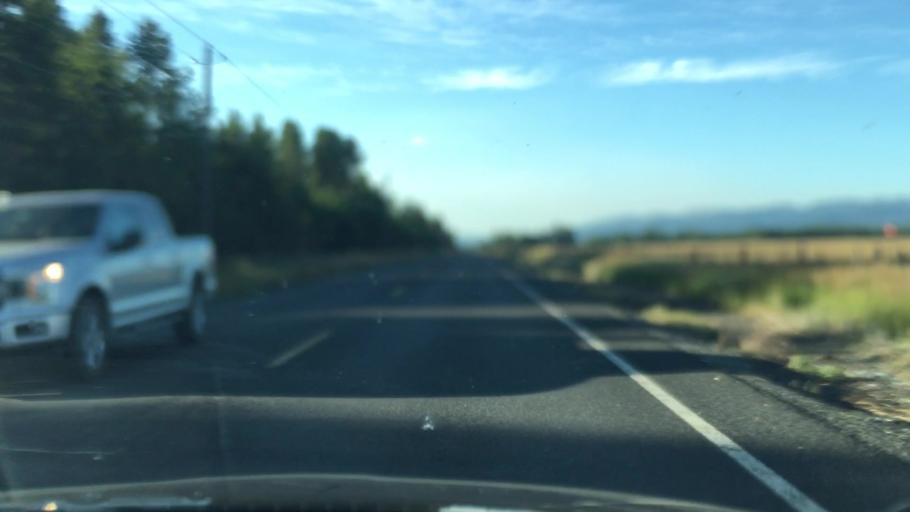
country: US
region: Idaho
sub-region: Valley County
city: McCall
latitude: 44.7778
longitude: -116.0771
